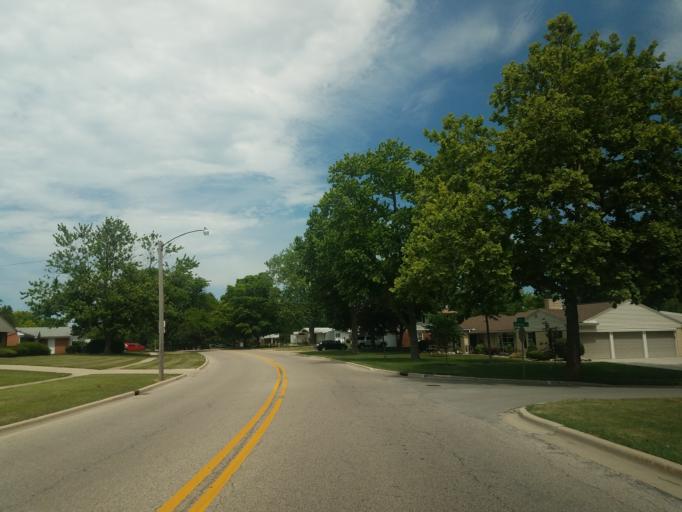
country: US
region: Illinois
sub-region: McLean County
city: Bloomington
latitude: 40.4912
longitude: -88.9615
